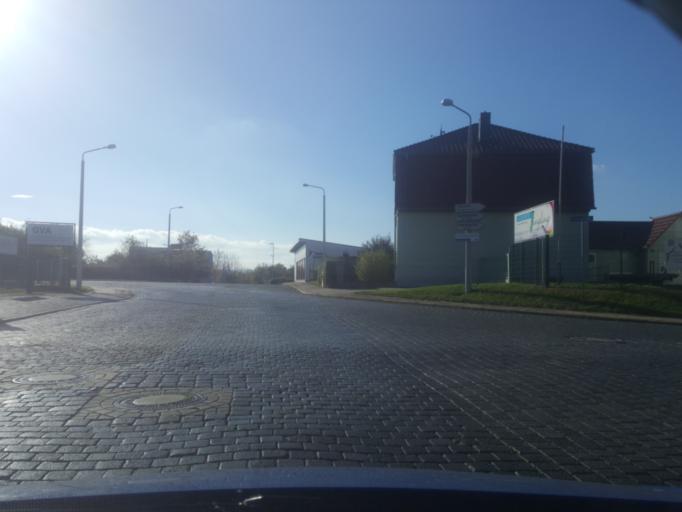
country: DE
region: Saxony-Anhalt
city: Sangerhausen
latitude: 51.4825
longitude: 11.3031
